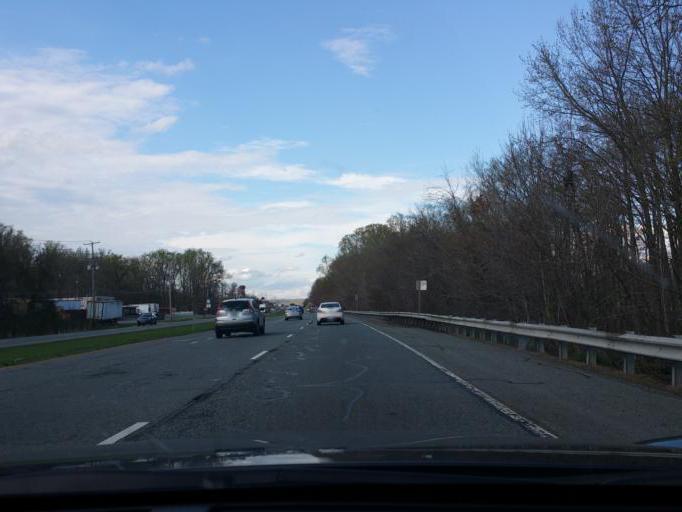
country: US
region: Maryland
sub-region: Harford County
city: Havre de Grace
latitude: 39.5385
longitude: -76.1123
